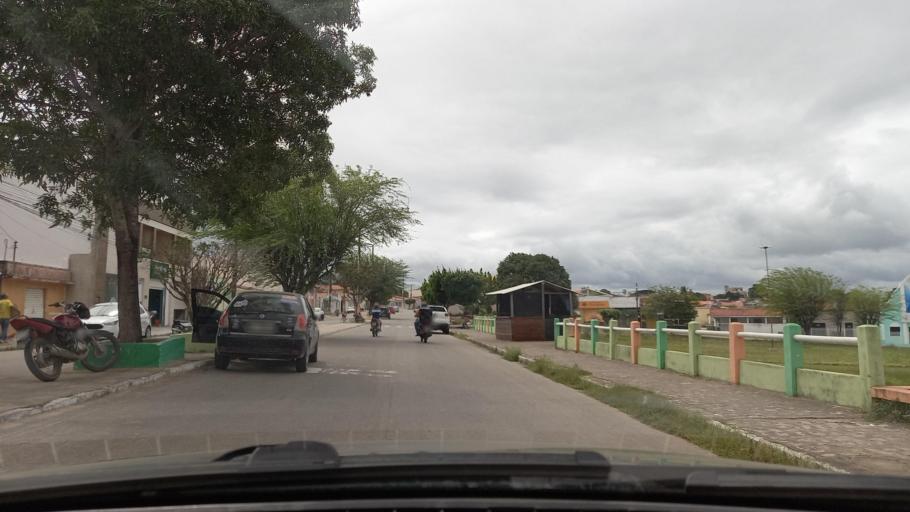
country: BR
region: Sergipe
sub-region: Caninde De Sao Francisco
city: Caninde de Sao Francisco
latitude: -9.6064
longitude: -37.7612
